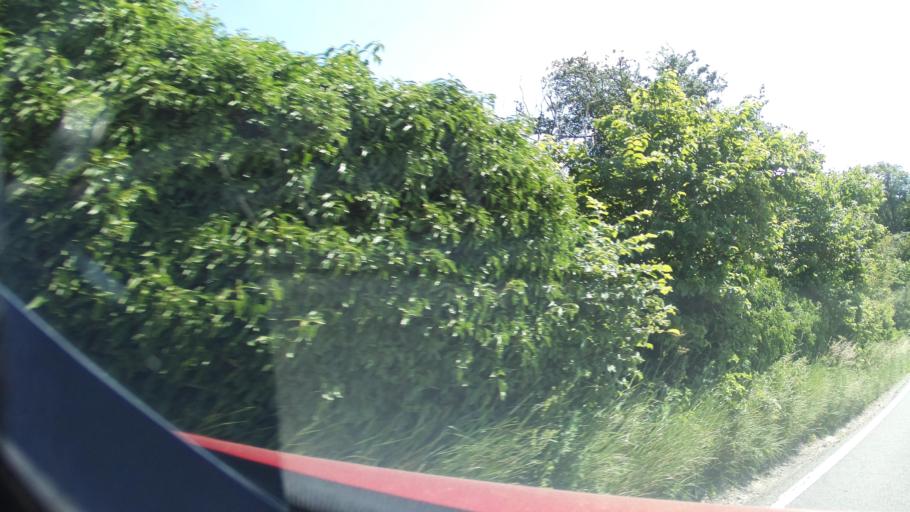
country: GB
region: England
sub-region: Derbyshire
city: Ashbourne
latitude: 53.0689
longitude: -1.7484
